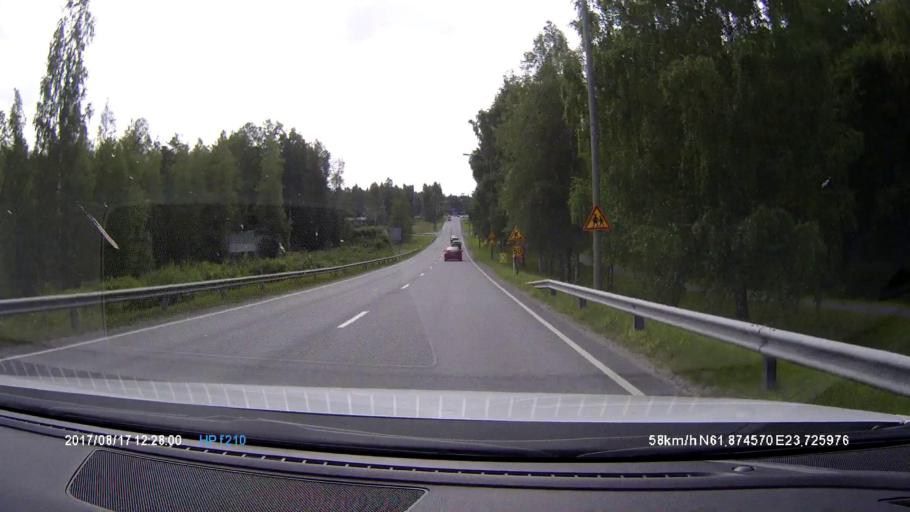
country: FI
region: Pirkanmaa
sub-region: Tampere
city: Kuru
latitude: 61.8742
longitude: 23.7261
